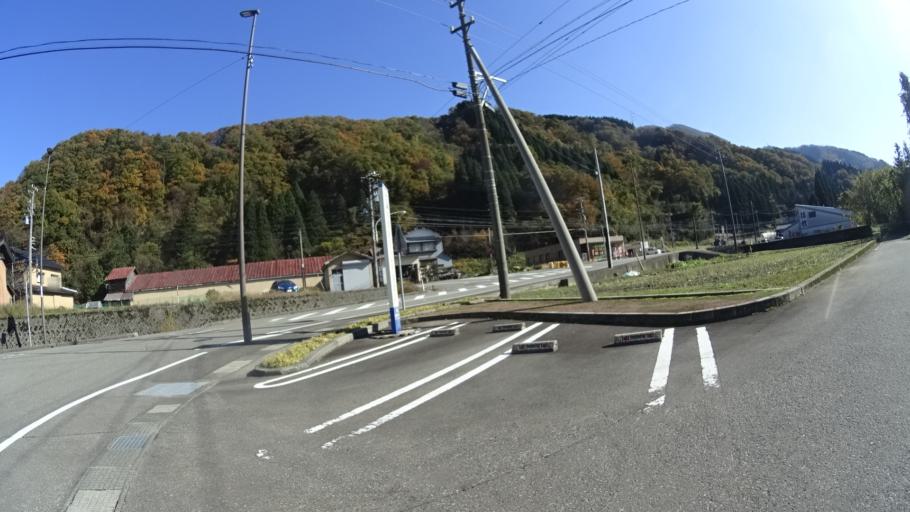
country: JP
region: Ishikawa
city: Tsurugi-asahimachi
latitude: 36.3447
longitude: 136.6312
